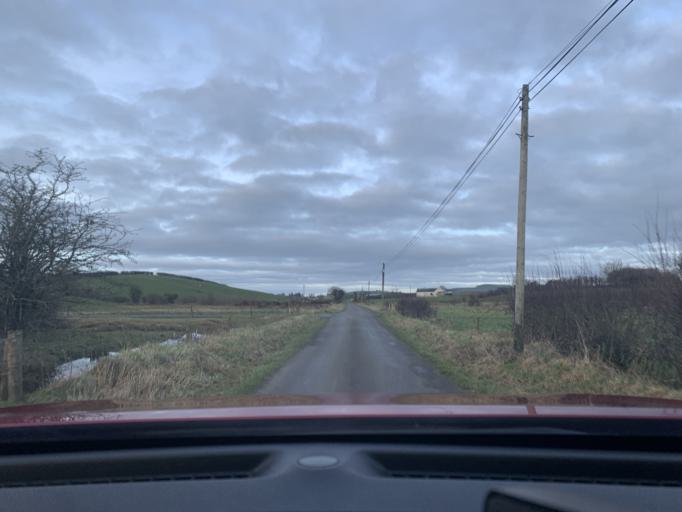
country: IE
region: Connaught
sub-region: Sligo
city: Ballymote
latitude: 54.0502
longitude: -8.5704
